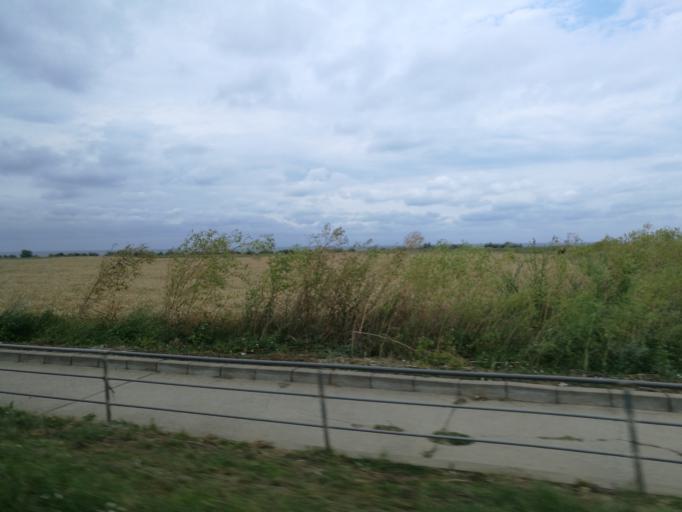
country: RO
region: Constanta
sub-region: Municipiul Mangalia
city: Mangalia
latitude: 43.7676
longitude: 28.5747
